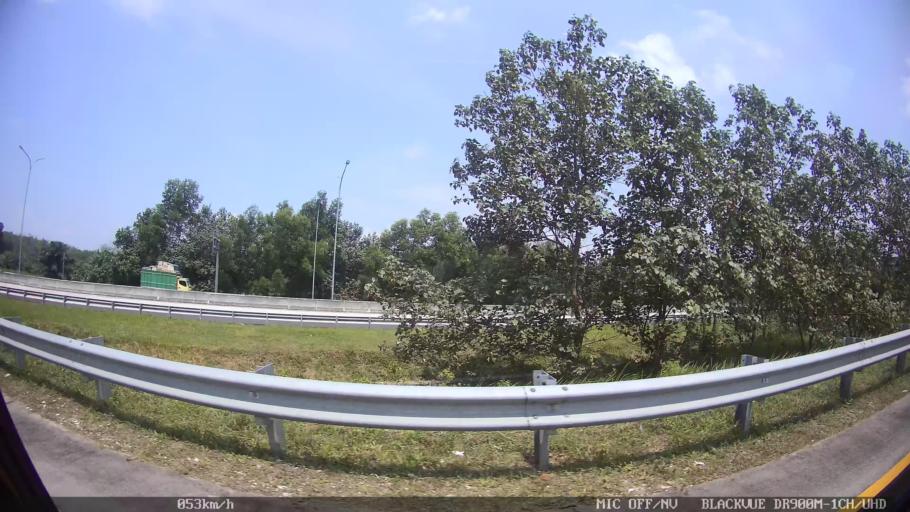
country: ID
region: Lampung
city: Kedaton
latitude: -5.3668
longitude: 105.3258
